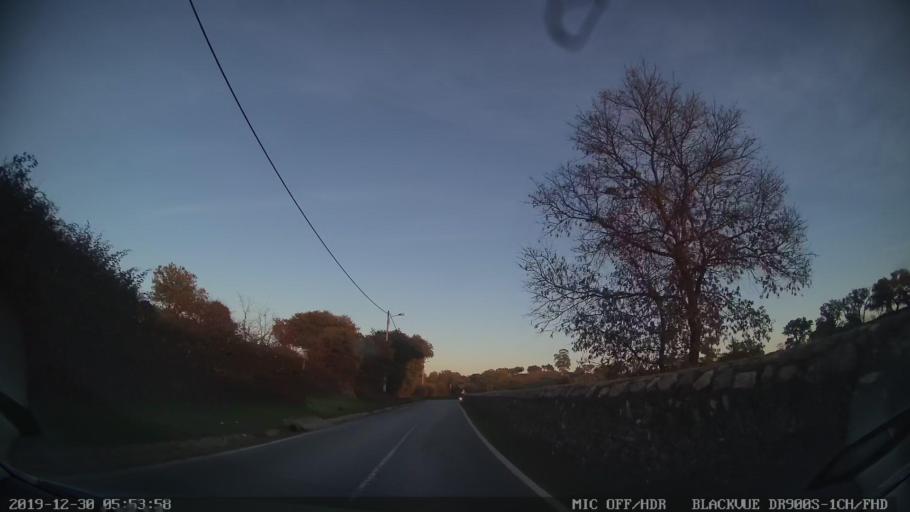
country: PT
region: Castelo Branco
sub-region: Idanha-A-Nova
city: Idanha-a-Nova
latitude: 40.0189
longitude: -7.2484
